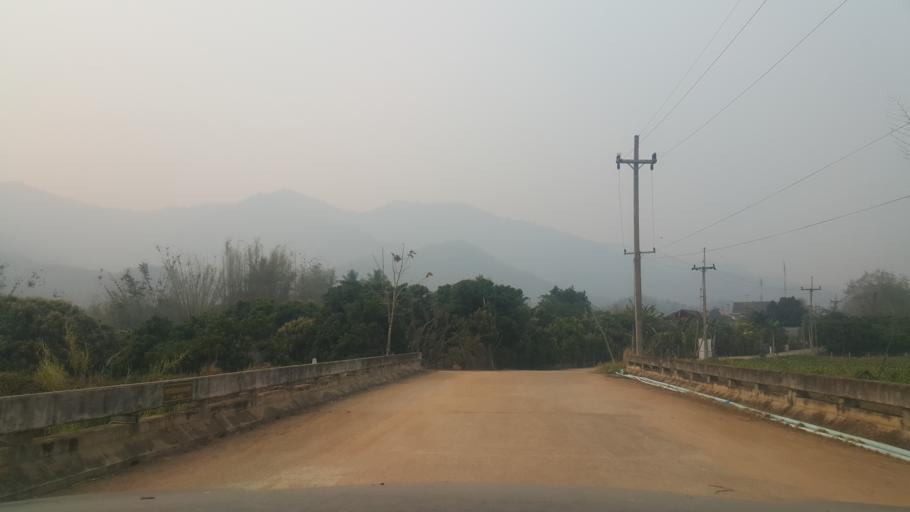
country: TH
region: Lamphun
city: Mae Tha
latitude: 18.5085
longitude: 99.2129
